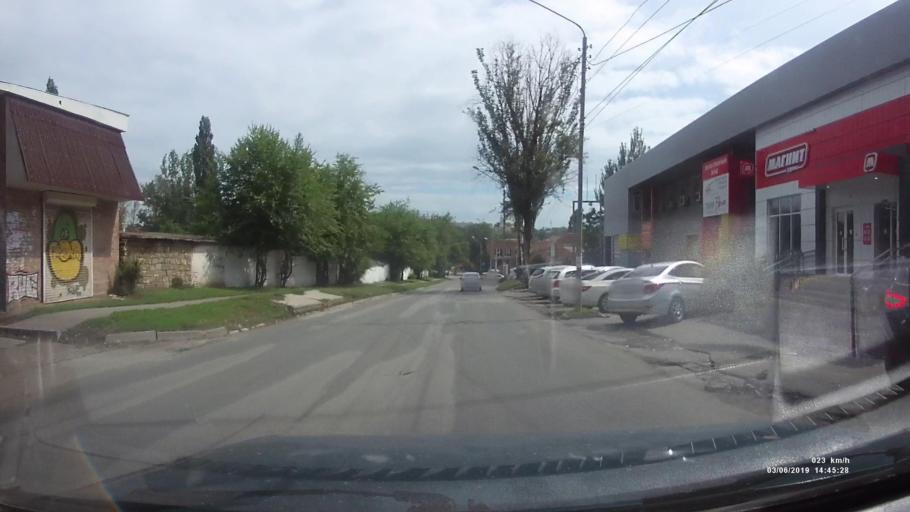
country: RU
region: Rostov
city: Rostov-na-Donu
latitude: 47.2483
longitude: 39.7232
